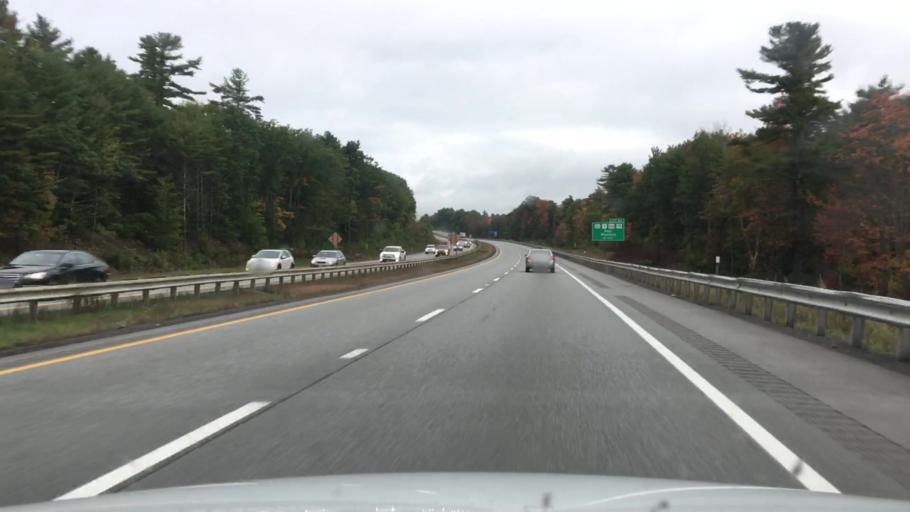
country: US
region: Maine
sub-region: Cumberland County
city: Cumberland Center
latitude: 43.8517
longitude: -70.3229
